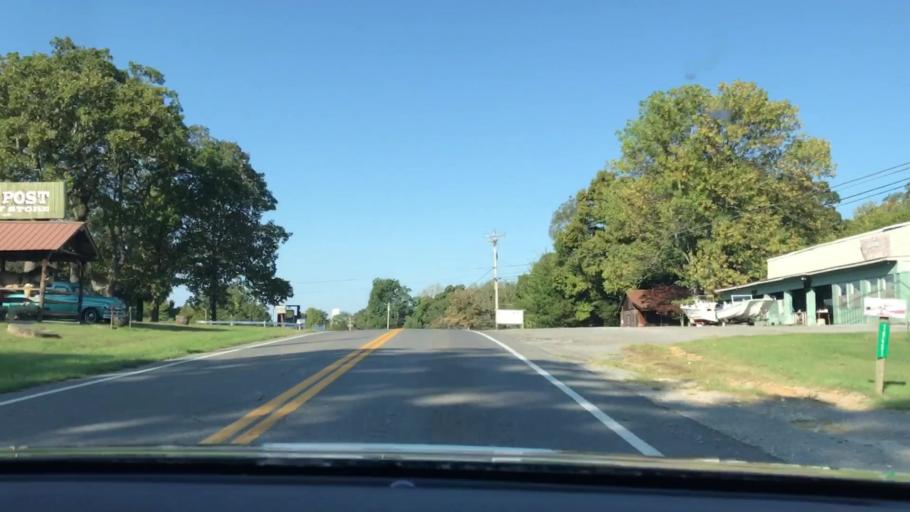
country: US
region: Kentucky
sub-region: Marshall County
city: Benton
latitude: 36.7772
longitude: -88.1487
